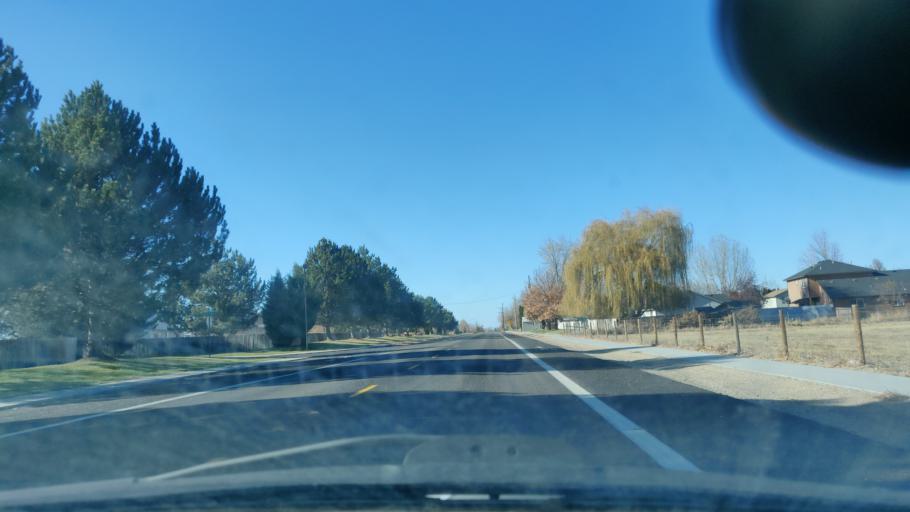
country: US
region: Idaho
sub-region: Ada County
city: Meridian
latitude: 43.6120
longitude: -116.4228
